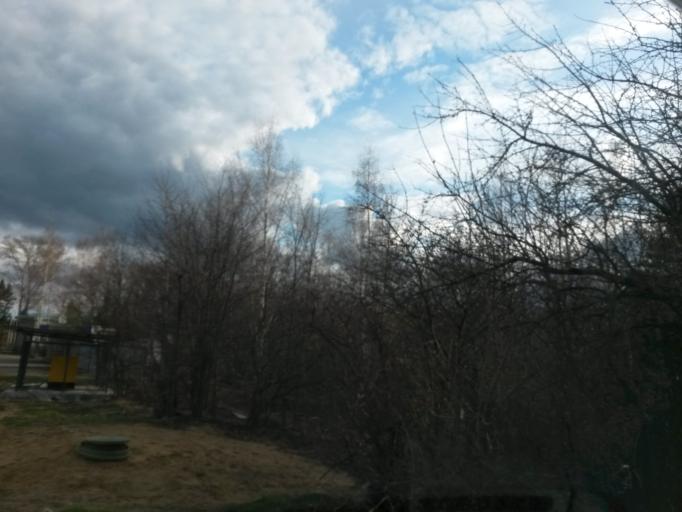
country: RU
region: Jaroslavl
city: Pereslavl'-Zalesskiy
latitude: 56.7082
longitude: 38.7990
